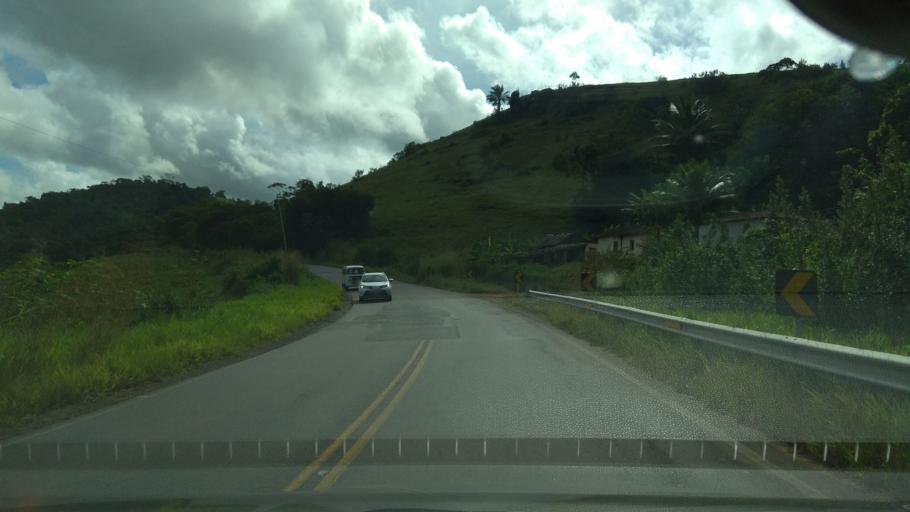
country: BR
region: Bahia
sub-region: Mutuipe
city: Mutuipe
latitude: -13.1893
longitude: -39.4414
